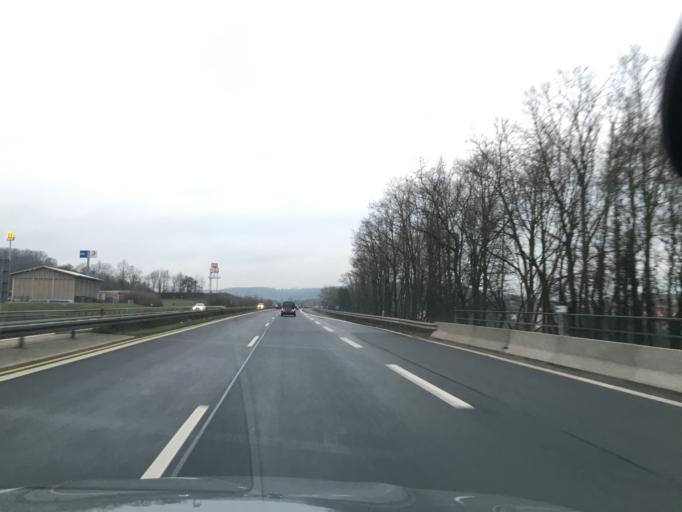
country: DE
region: Bavaria
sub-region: Regierungsbezirk Unterfranken
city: Geiselwind
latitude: 49.7701
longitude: 10.4759
